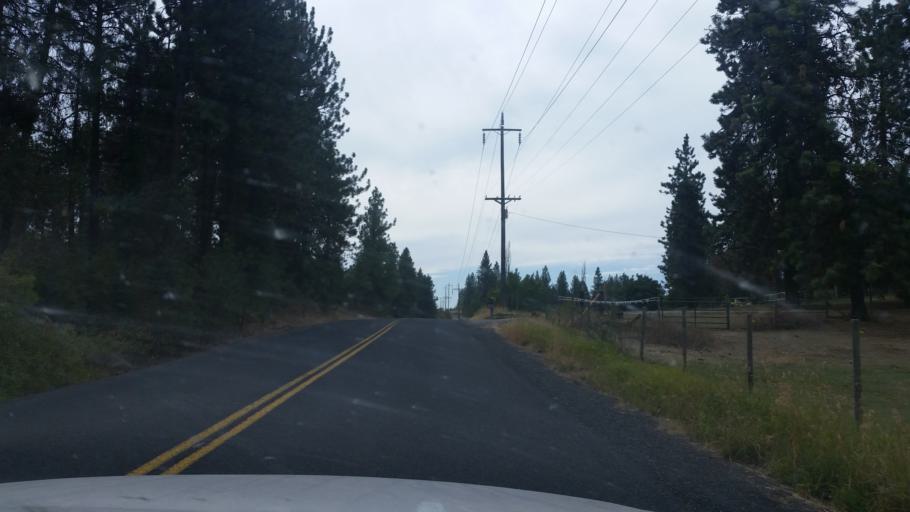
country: US
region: Washington
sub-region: Spokane County
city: Spokane
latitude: 47.6497
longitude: -117.4967
